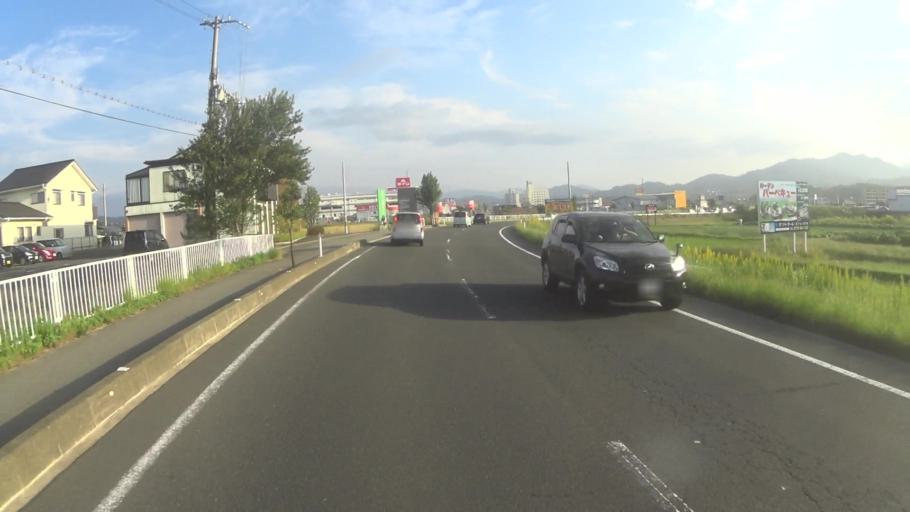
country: JP
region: Kyoto
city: Miyazu
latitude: 35.6120
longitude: 135.0801
